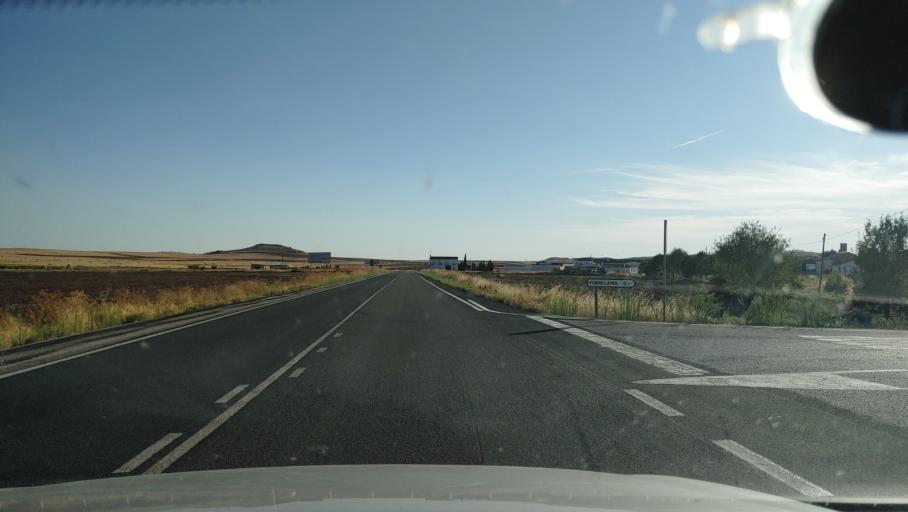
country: ES
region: Castille-La Mancha
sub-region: Provincia de Ciudad Real
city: Fuenllana
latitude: 38.7566
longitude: -2.9516
